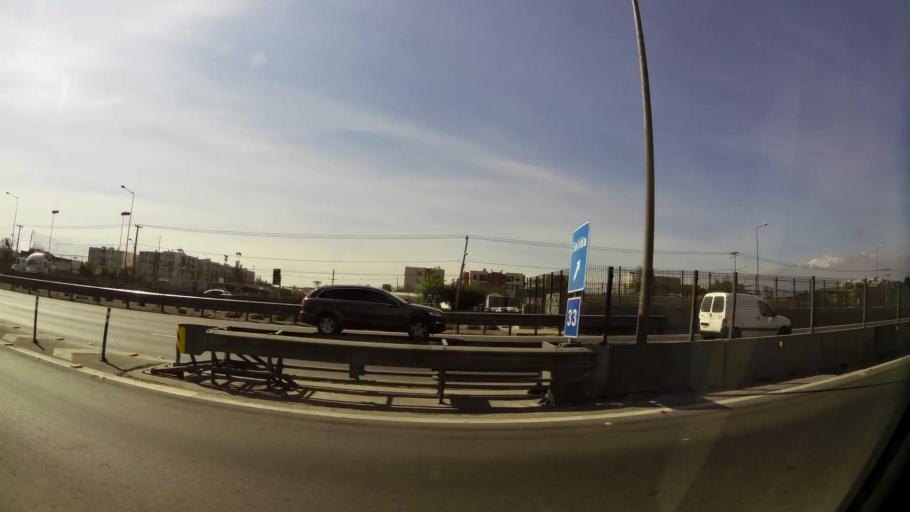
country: CL
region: Santiago Metropolitan
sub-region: Provincia de Santiago
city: La Pintana
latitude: -33.5361
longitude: -70.6689
